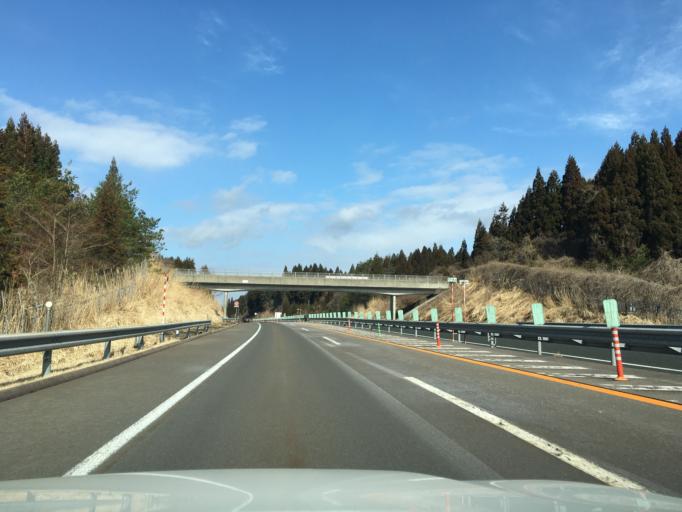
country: JP
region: Akita
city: Akita
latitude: 39.7281
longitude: 140.1801
